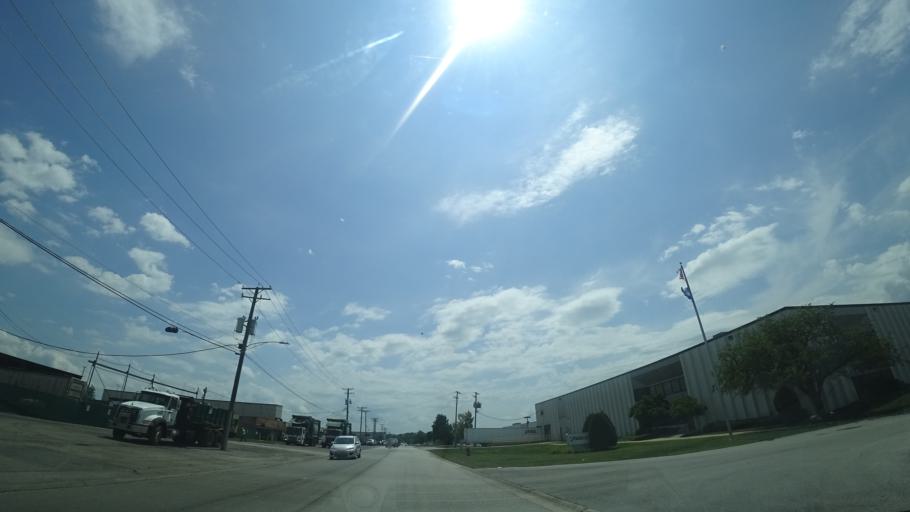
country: US
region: Illinois
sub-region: Cook County
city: Chicago Ridge
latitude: 41.6818
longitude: -87.7687
